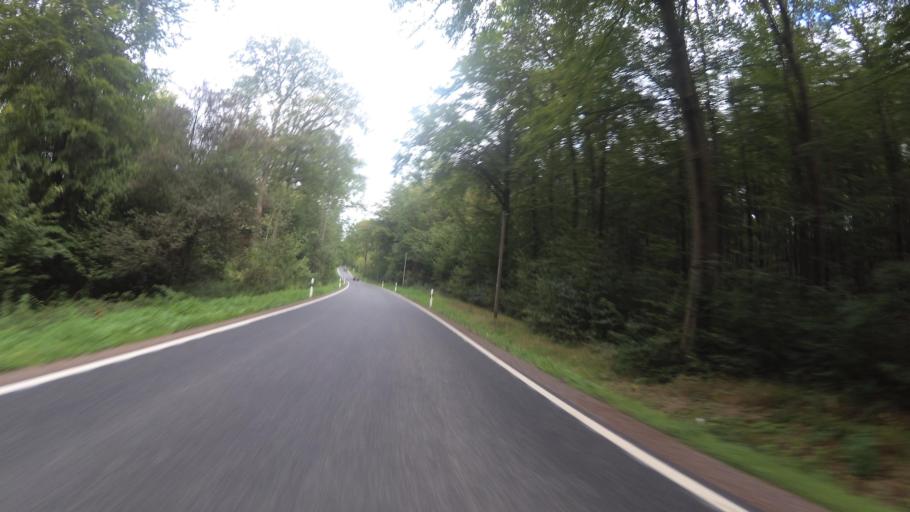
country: DE
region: Saarland
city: Riegelsberg
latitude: 49.2710
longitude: 6.9240
